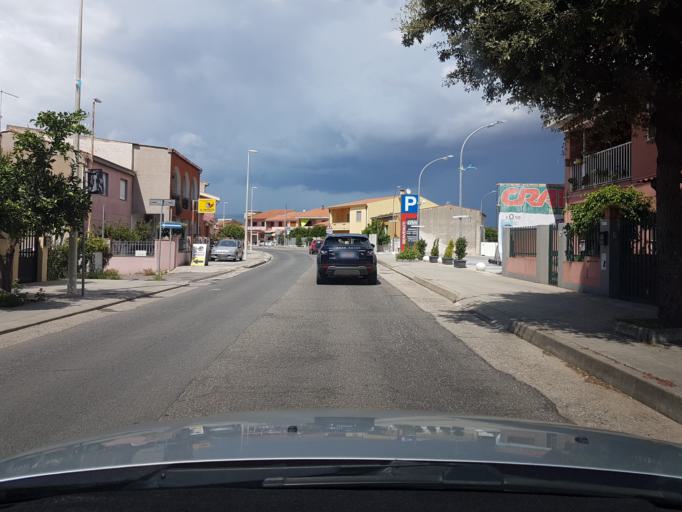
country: IT
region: Sardinia
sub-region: Provincia di Oristano
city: Riola Sardo
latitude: 39.9899
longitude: 8.5415
